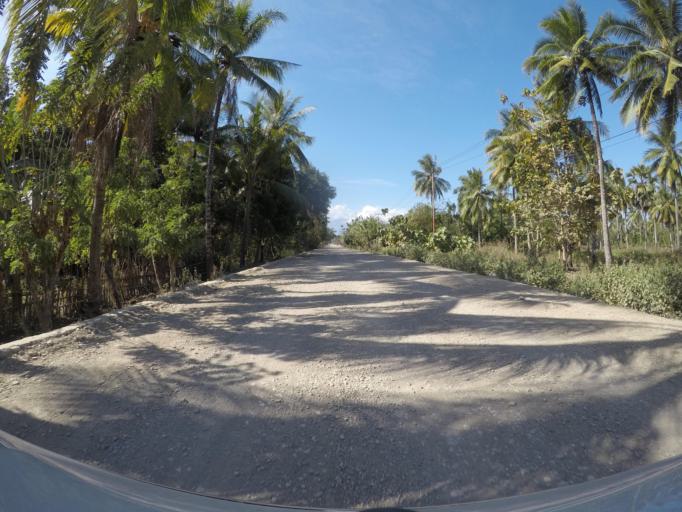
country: TL
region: Viqueque
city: Viqueque
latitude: -8.8562
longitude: 126.5107
